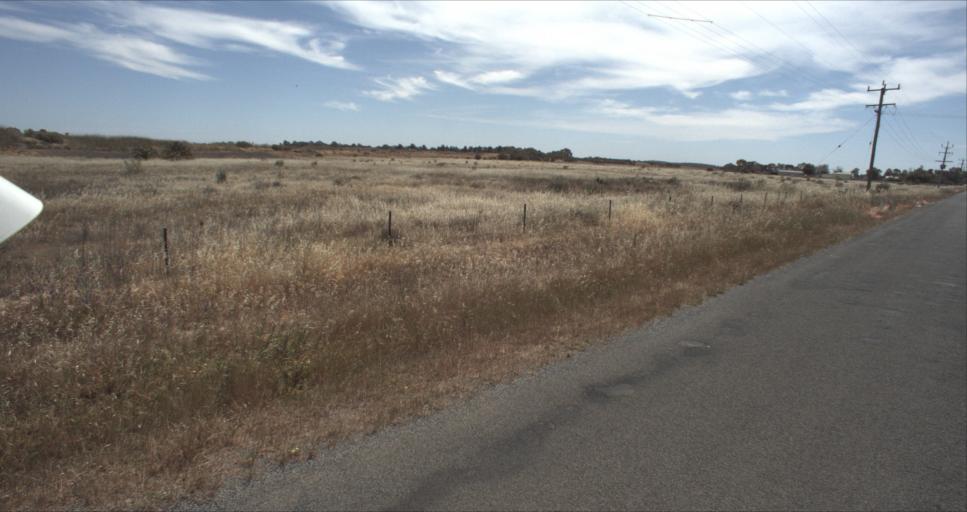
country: AU
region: New South Wales
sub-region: Leeton
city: Leeton
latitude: -34.6067
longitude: 146.4259
